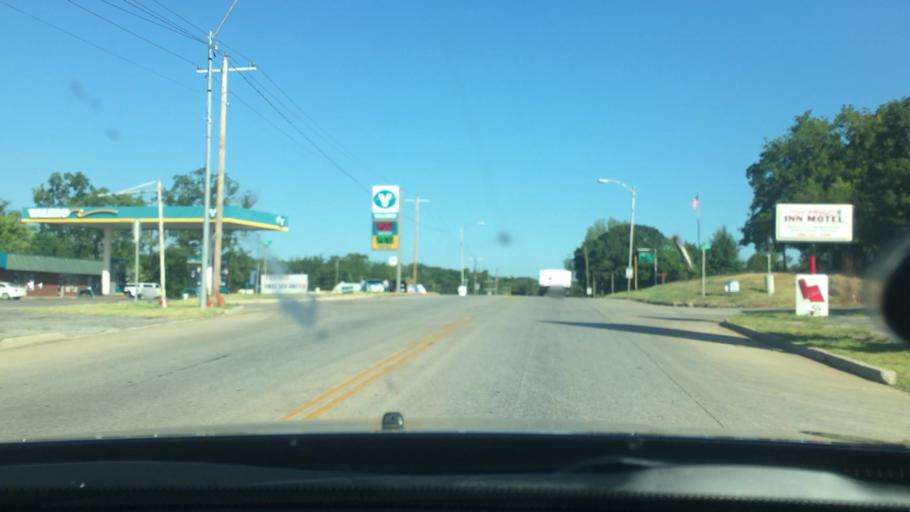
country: US
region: Oklahoma
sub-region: Johnston County
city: Tishomingo
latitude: 34.2376
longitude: -96.6824
